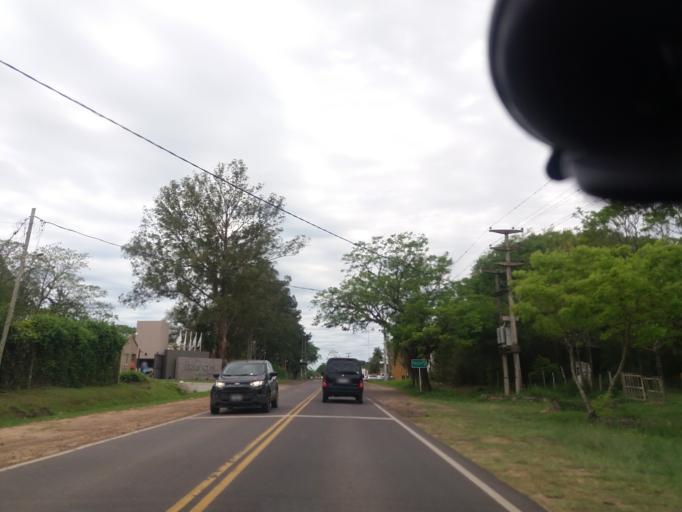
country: AR
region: Corrientes
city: Corrientes
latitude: -27.4511
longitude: -58.7346
